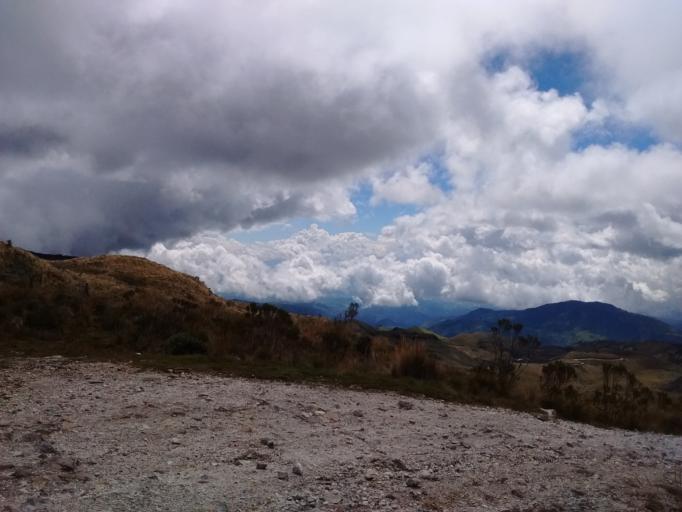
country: CO
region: Cauca
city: Totoro
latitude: 2.3335
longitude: -76.3944
